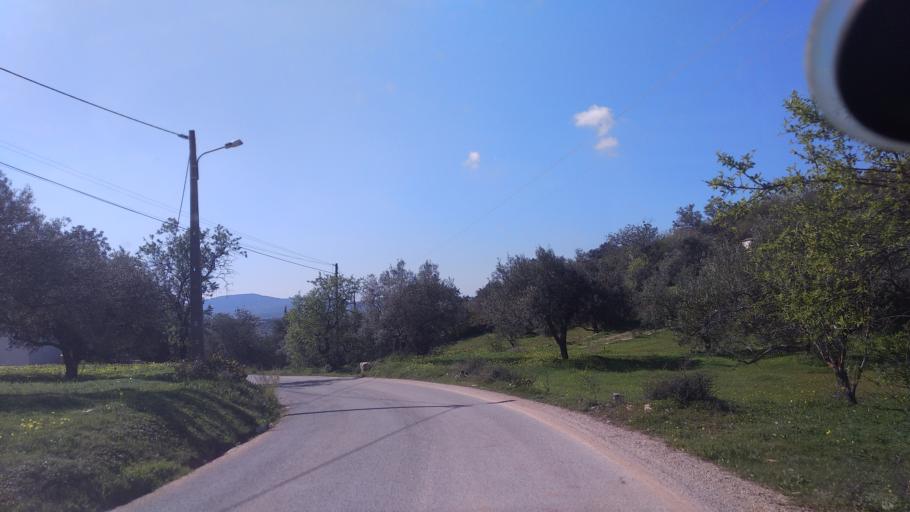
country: PT
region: Faro
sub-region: Sao Bras de Alportel
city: Sao Bras de Alportel
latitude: 37.1372
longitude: -7.9095
